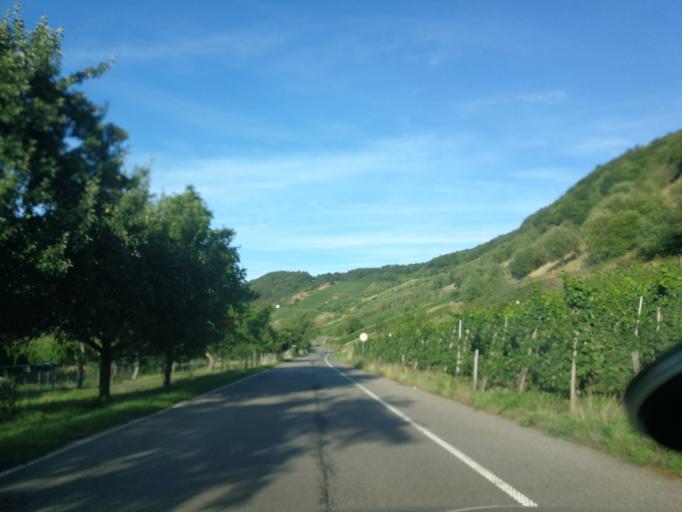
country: DE
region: Rheinland-Pfalz
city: Kenn
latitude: 49.8027
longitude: 6.7329
